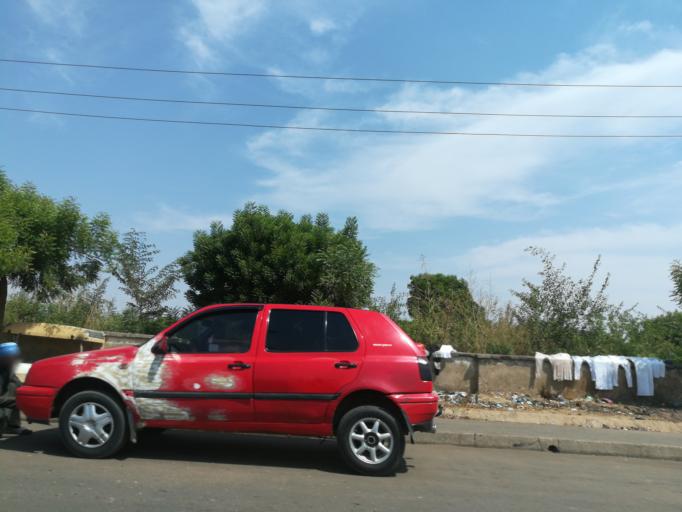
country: NG
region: Kano
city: Kano
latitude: 12.0205
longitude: 8.5187
